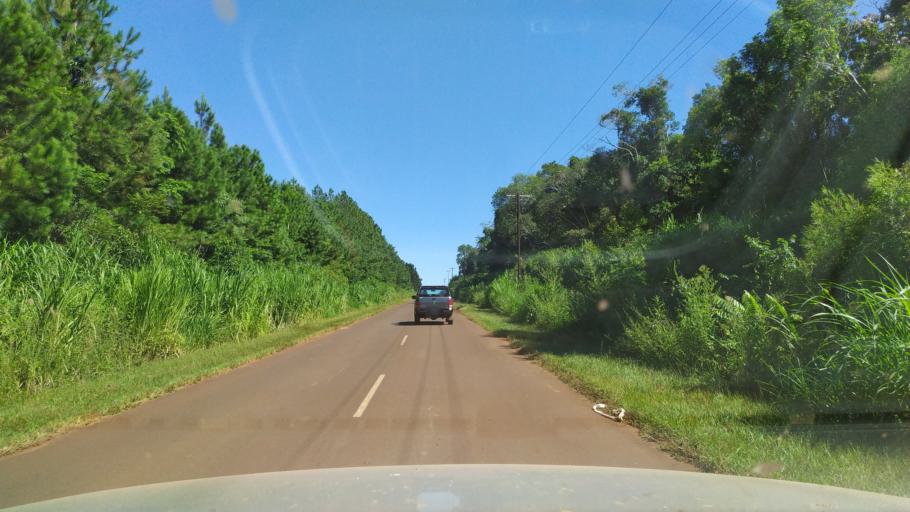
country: AR
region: Misiones
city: Caraguatay
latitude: -26.6768
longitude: -54.7200
